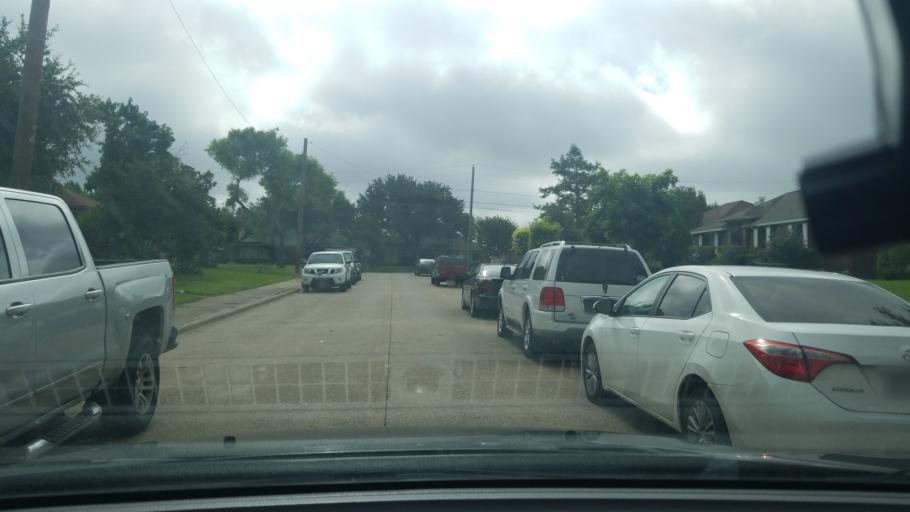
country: US
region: Texas
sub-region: Dallas County
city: Balch Springs
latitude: 32.7893
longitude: -96.6876
